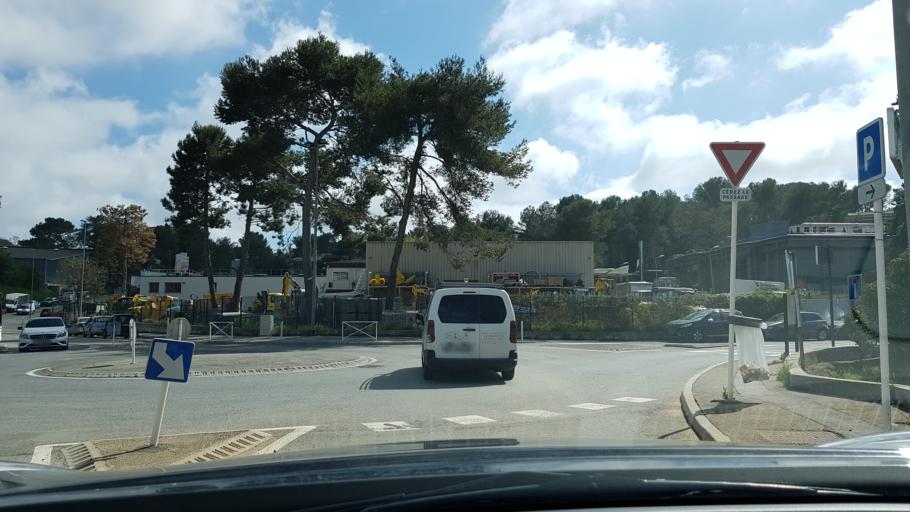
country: FR
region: Provence-Alpes-Cote d'Azur
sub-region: Departement des Alpes-Maritimes
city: Biot
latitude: 43.6054
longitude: 7.0761
